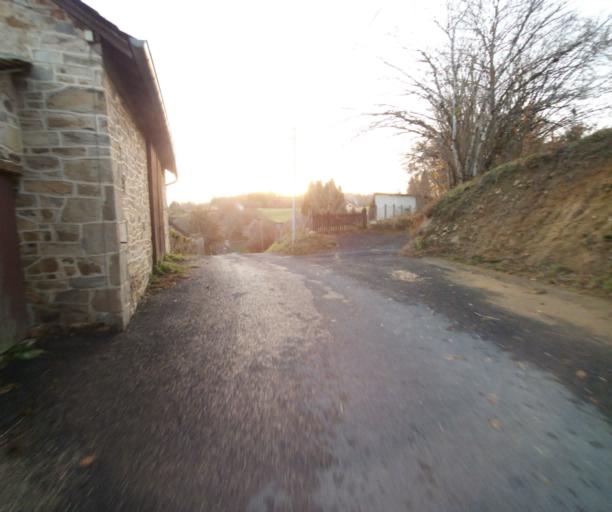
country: FR
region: Limousin
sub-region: Departement de la Correze
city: Laguenne
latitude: 45.2362
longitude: 1.7705
